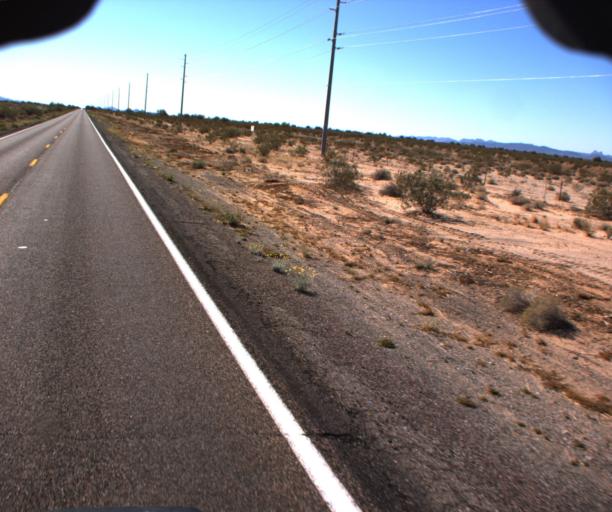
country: US
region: Arizona
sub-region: La Paz County
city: Quartzsite
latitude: 33.8871
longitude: -113.9545
